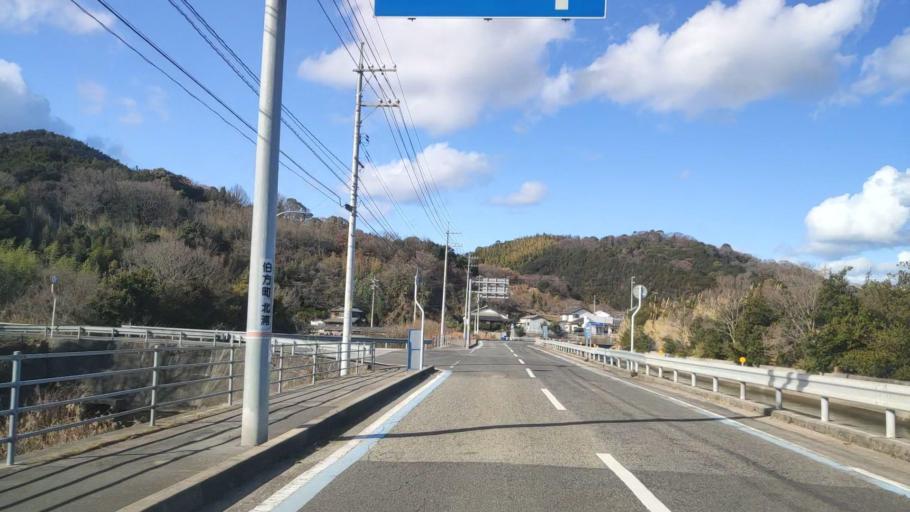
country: JP
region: Hiroshima
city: Innoshima
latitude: 34.2170
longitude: 133.1071
